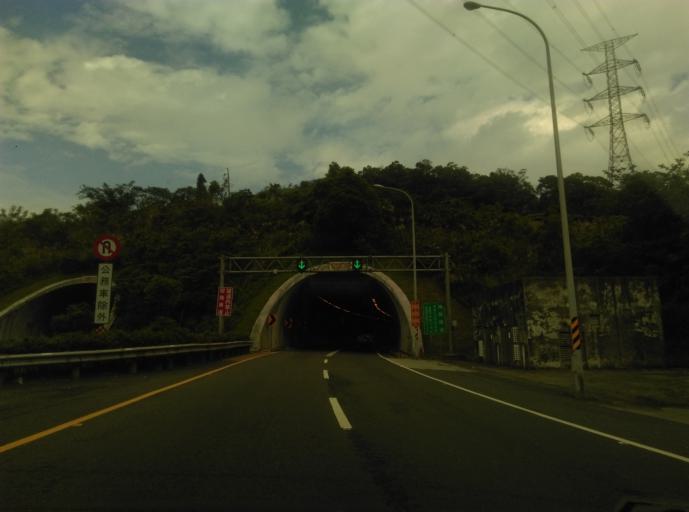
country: TW
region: Taiwan
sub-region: Keelung
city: Keelung
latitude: 25.1287
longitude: 121.6970
